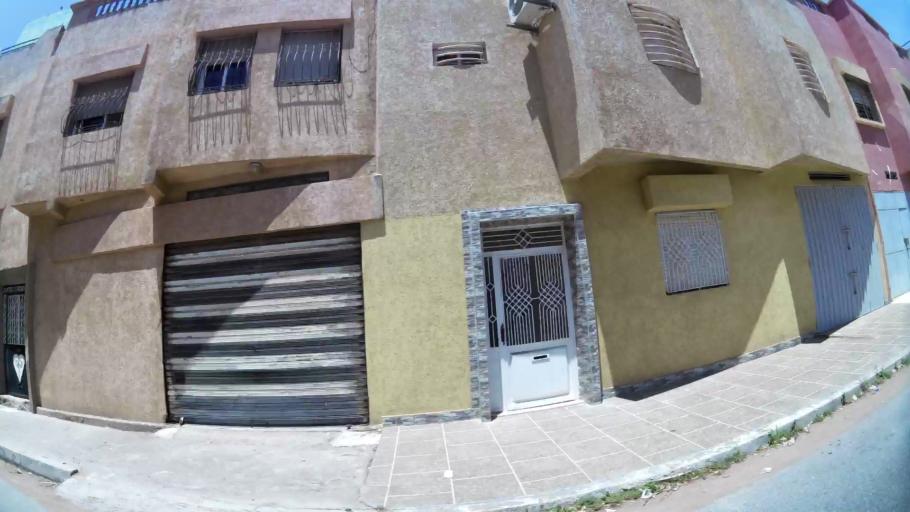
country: MA
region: Gharb-Chrarda-Beni Hssen
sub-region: Kenitra Province
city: Kenitra
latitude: 34.2505
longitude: -6.6199
